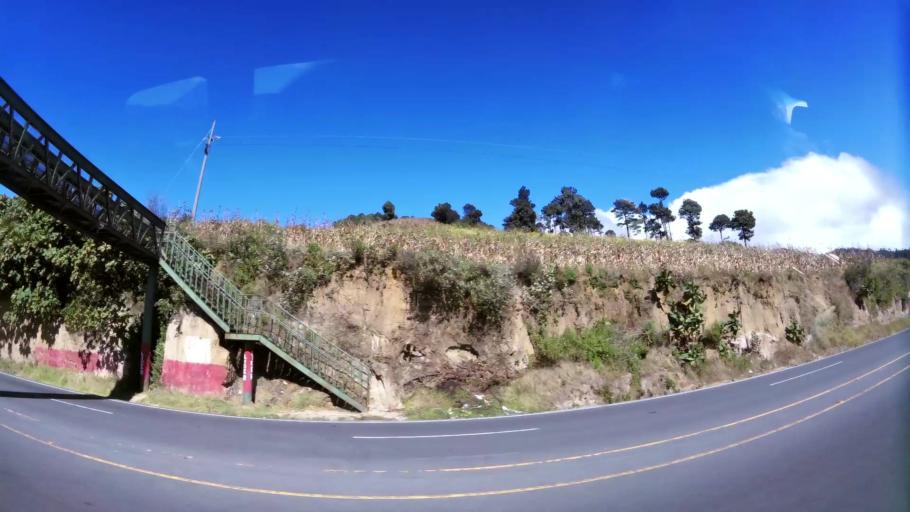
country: GT
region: Solola
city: Solola
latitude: 14.8212
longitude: -91.1999
